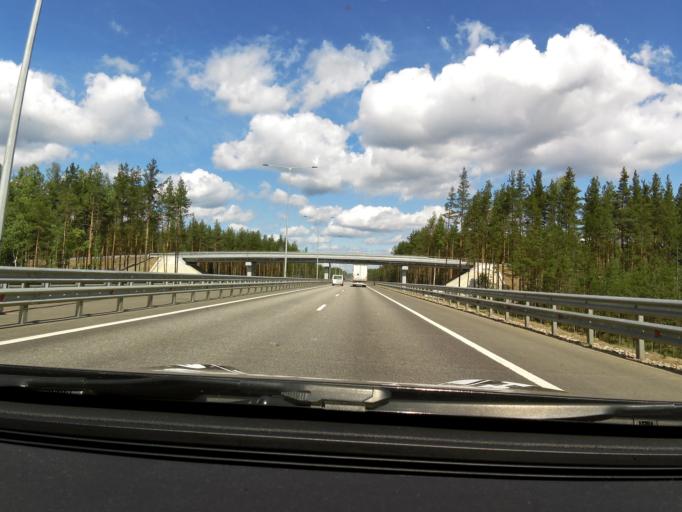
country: RU
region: Tverskaya
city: Krasnomayskiy
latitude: 57.5692
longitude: 34.2618
